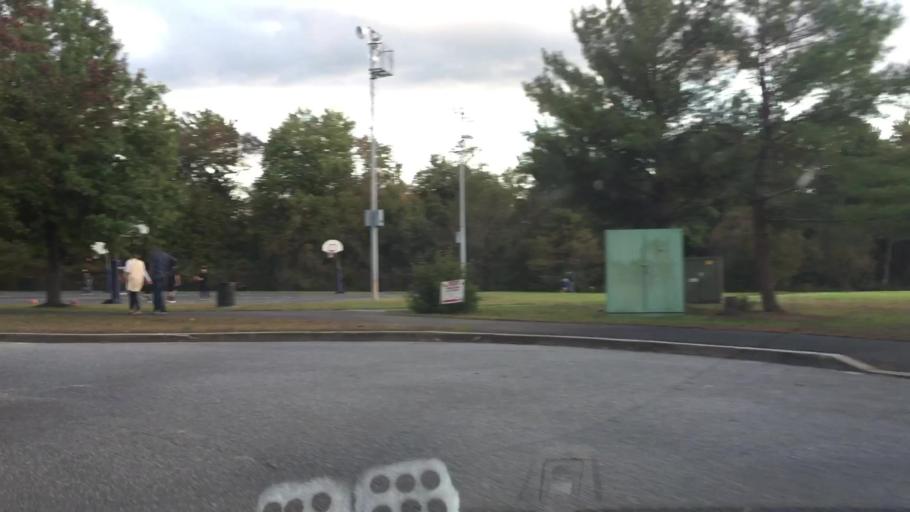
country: US
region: New Jersey
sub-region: Gloucester County
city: Pitman
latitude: 39.7412
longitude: -75.0945
